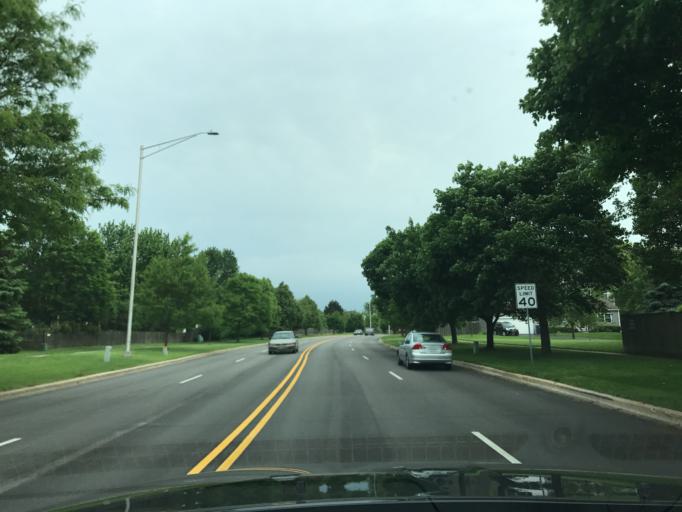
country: US
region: Illinois
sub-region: DuPage County
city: Woodridge
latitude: 41.7422
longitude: -88.1030
